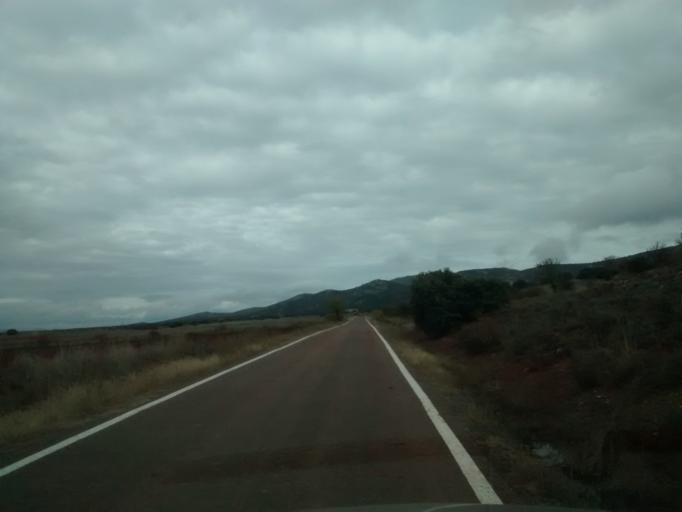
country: ES
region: Aragon
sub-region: Provincia de Teruel
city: Tornos
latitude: 40.9787
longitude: -1.4651
